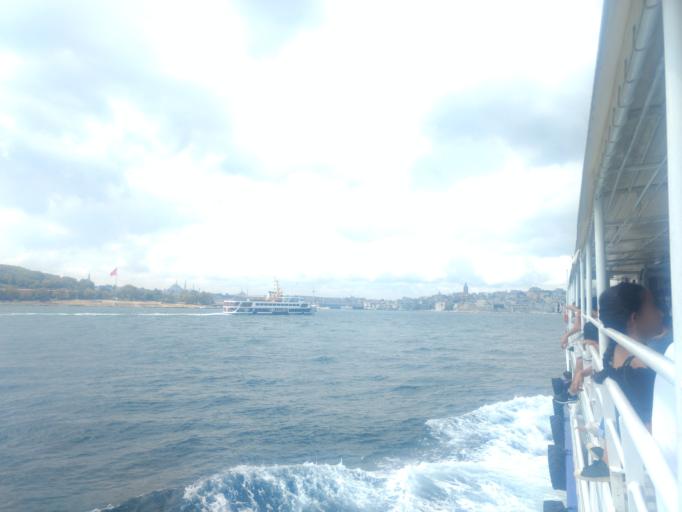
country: TR
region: Istanbul
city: Eminoenue
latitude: 41.0173
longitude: 28.9954
